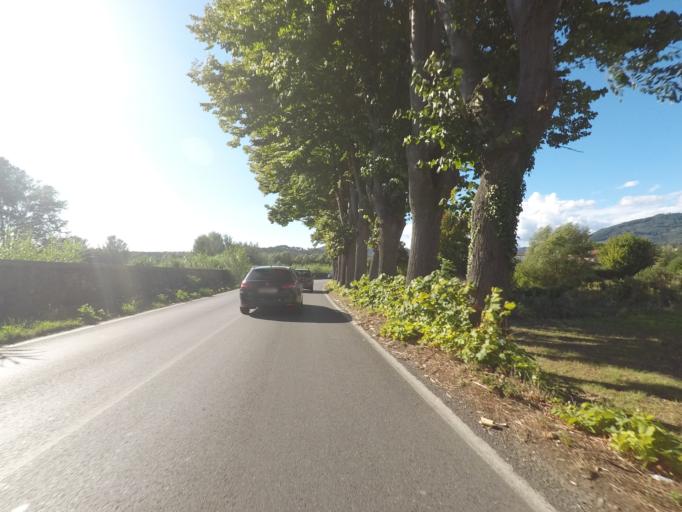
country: IT
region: Tuscany
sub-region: Provincia di Lucca
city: Lucca
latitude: 43.8735
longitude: 10.4941
